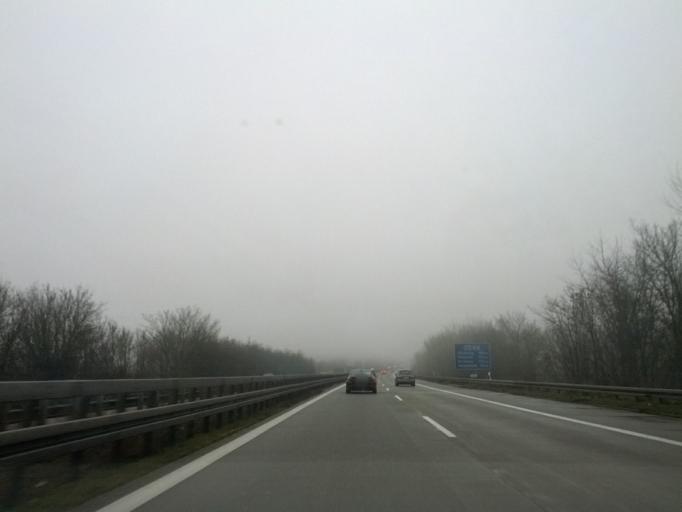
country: DE
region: Baden-Wuerttemberg
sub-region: Tuebingen Region
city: Langenau
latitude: 48.4982
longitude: 10.0850
